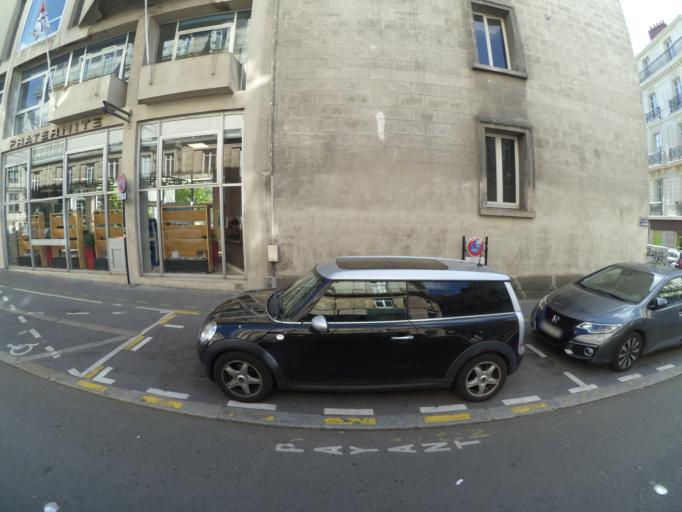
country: FR
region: Pays de la Loire
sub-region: Departement de la Loire-Atlantique
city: Nantes
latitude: 47.2189
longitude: -1.5537
